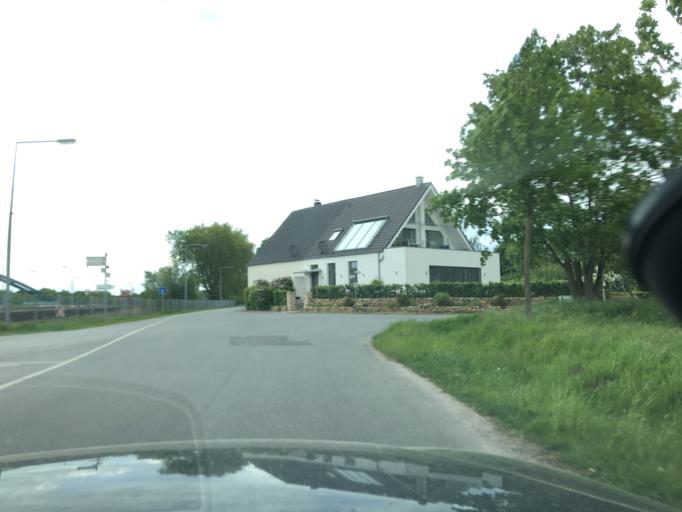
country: DE
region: North Rhine-Westphalia
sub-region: Regierungsbezirk Munster
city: Muenster
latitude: 51.9779
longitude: 7.6637
